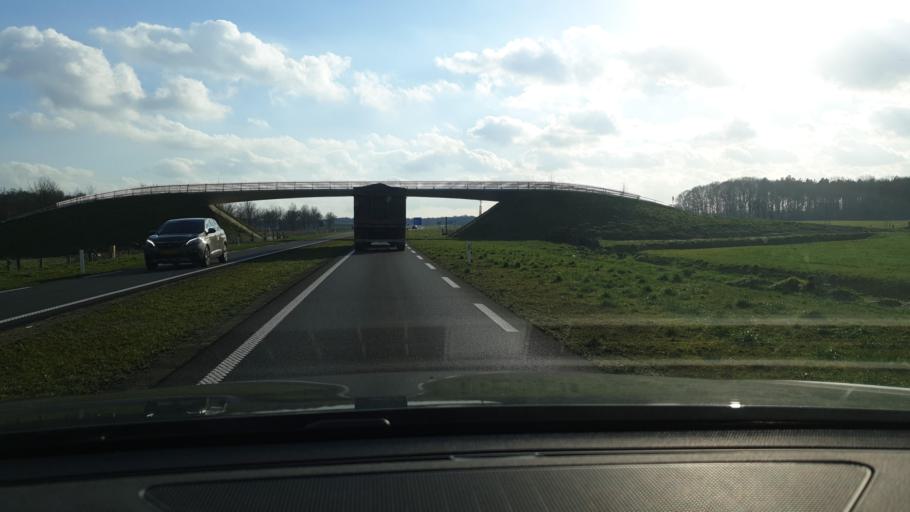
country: NL
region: North Brabant
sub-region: Gemeente Valkenswaard
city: Valkenswaard
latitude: 51.3495
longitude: 5.4188
